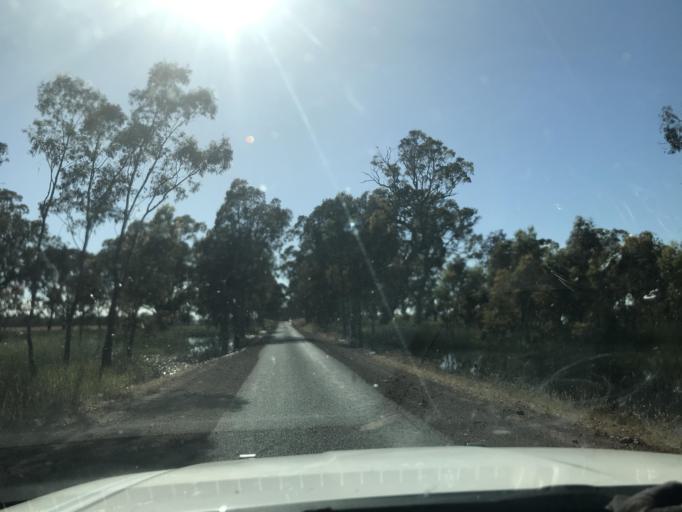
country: AU
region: Victoria
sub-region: Horsham
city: Horsham
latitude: -37.0249
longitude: 141.7021
